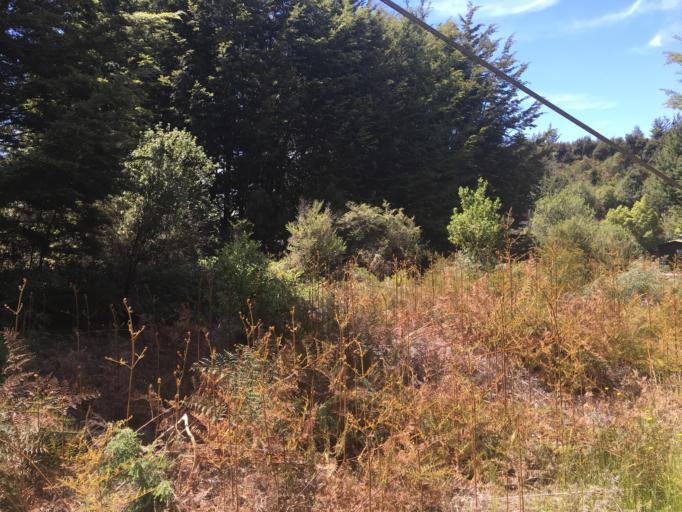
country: NZ
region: Southland
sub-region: Southland District
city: Te Anau
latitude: -45.4913
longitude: 167.6632
